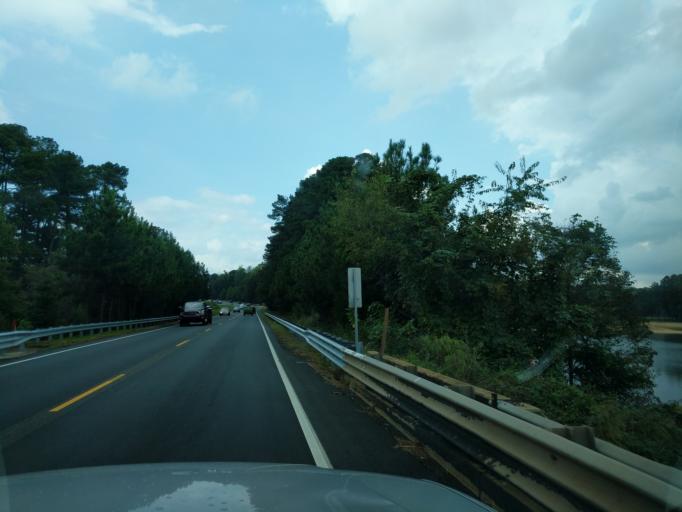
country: US
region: South Carolina
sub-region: Anderson County
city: Northlake
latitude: 34.5695
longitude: -82.6878
